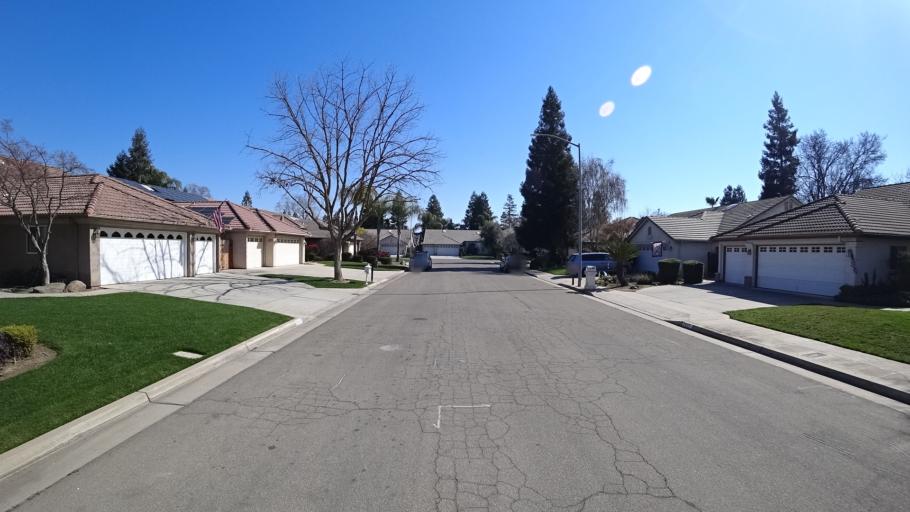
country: US
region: California
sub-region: Fresno County
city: Clovis
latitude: 36.8799
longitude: -119.7540
